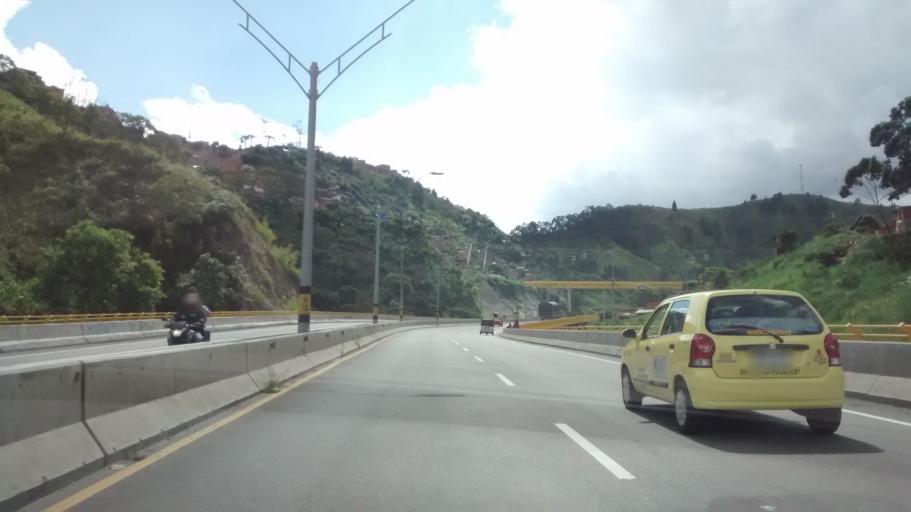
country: CO
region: Antioquia
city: Medellin
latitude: 6.2765
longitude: -75.6104
